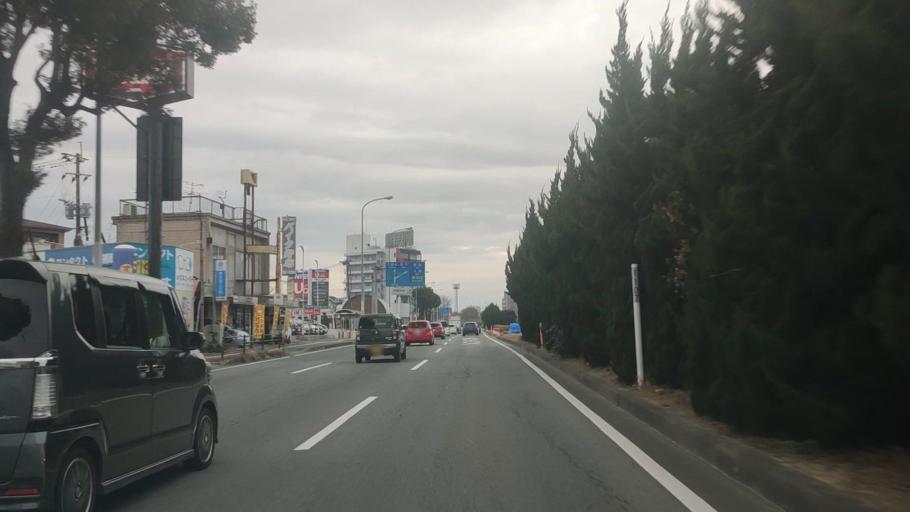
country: JP
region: Kumamoto
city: Kumamoto
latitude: 32.8129
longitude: 130.7498
